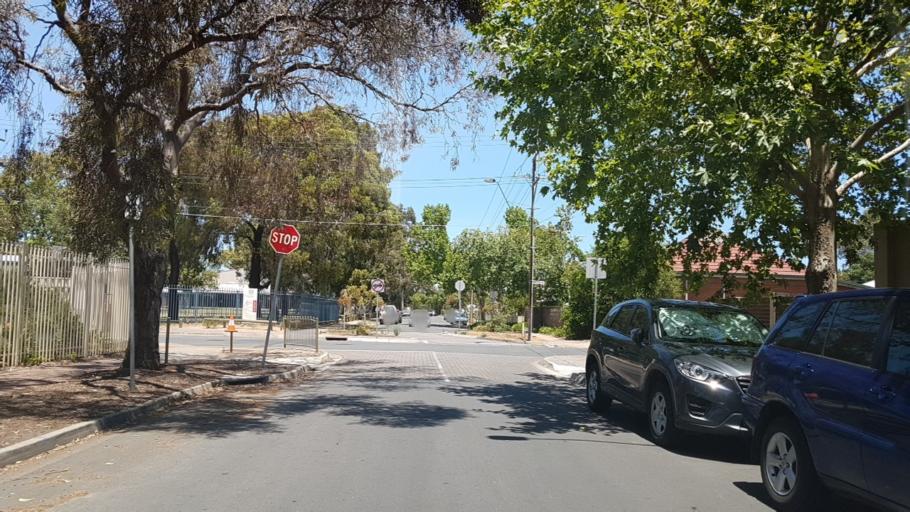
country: AU
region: South Australia
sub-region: City of West Torrens
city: Thebarton
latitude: -34.9161
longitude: 138.5618
